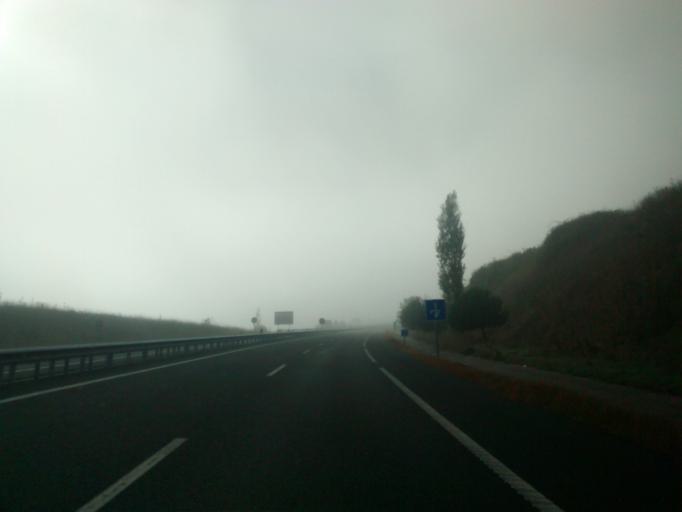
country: ES
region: Cantabria
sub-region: Provincia de Cantabria
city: Arenas de Iguna
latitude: 43.1742
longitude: -4.0543
